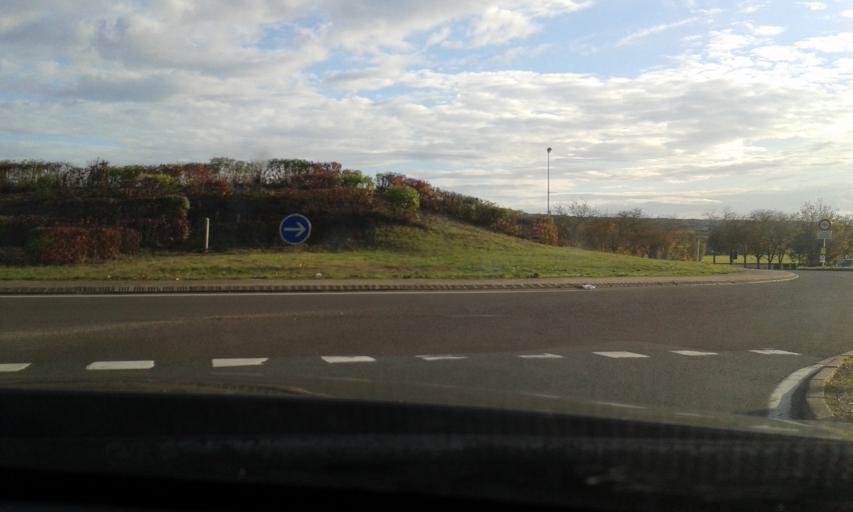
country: FR
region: Centre
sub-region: Departement d'Eure-et-Loir
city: Garnay
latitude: 48.7198
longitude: 1.3481
